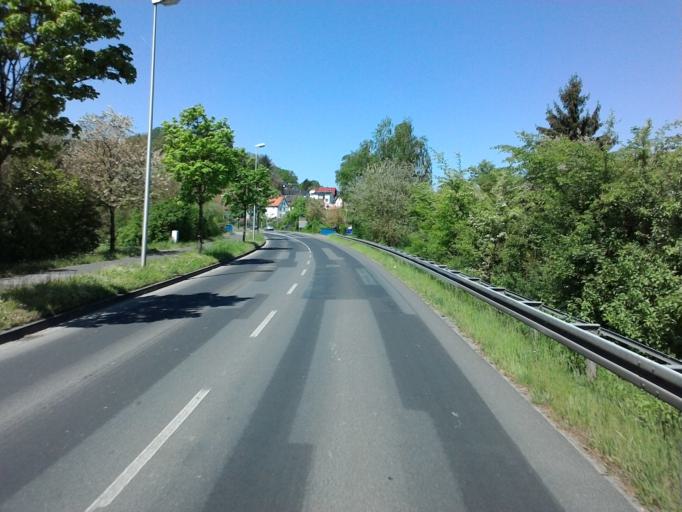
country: DE
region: Bavaria
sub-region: Regierungsbezirk Unterfranken
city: Lohr am Main
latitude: 49.9924
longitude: 9.5717
